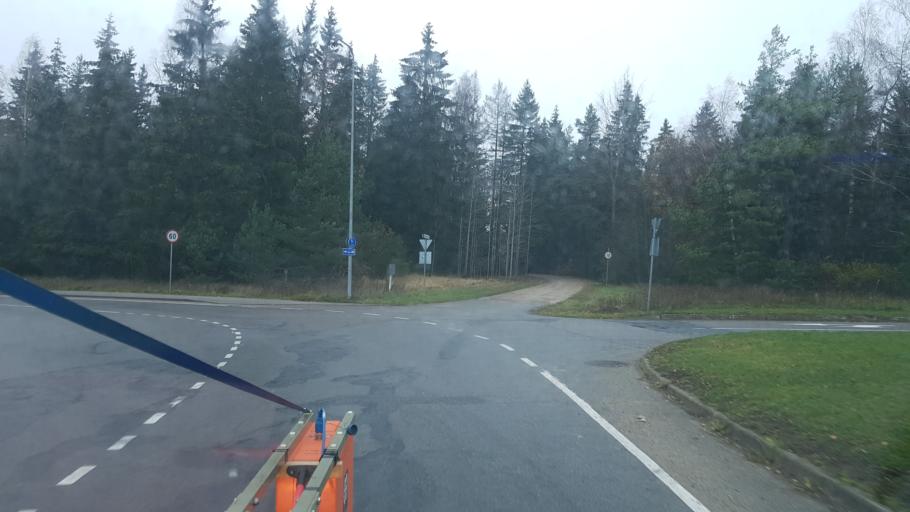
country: EE
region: Raplamaa
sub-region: Kohila vald
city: Kohila
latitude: 59.1813
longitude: 24.7810
